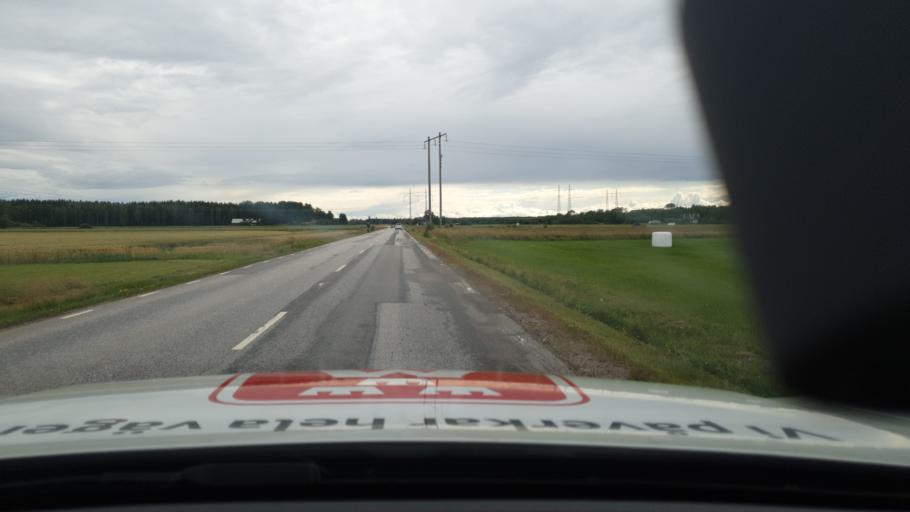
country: SE
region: Vaestra Goetaland
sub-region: Toreboda Kommun
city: Toereboda
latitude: 58.6950
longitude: 14.1316
